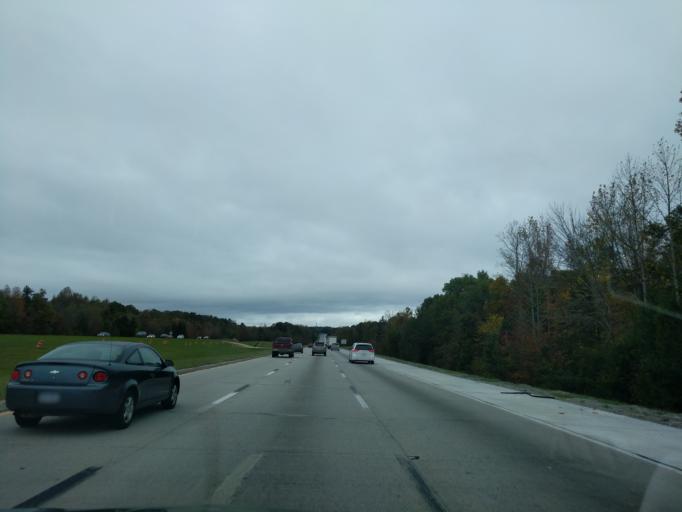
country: US
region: North Carolina
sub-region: Guilford County
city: Jamestown
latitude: 35.9631
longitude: -79.8936
